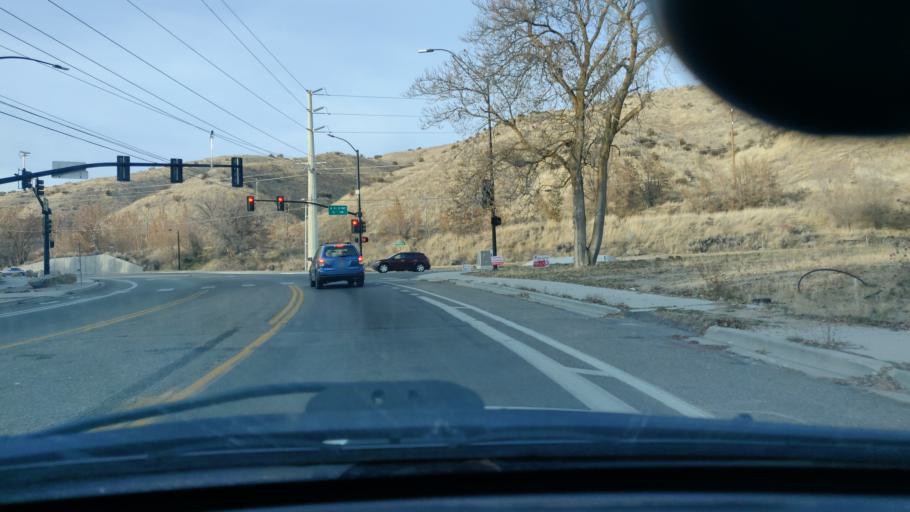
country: US
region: Idaho
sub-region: Ada County
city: Garden City
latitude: 43.6836
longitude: -116.2792
